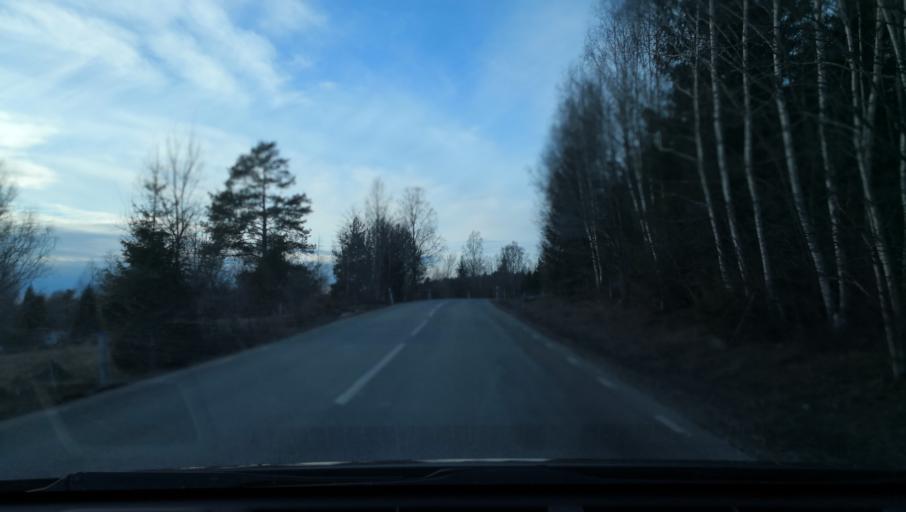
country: SE
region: Uppsala
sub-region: Osthammars Kommun
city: Gimo
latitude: 60.3373
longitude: 18.2193
